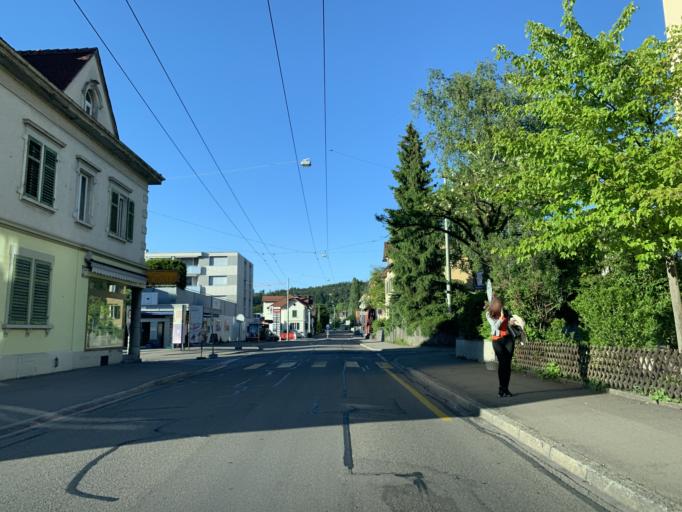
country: CH
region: Zurich
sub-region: Bezirk Winterthur
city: Seen (Kreis 3) / Bueelwiesen
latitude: 47.4840
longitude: 8.7626
